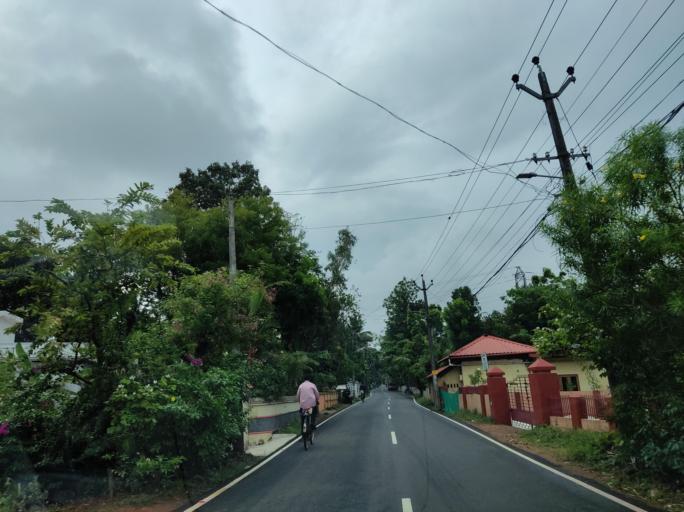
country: IN
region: Kerala
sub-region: Alappuzha
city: Mavelikara
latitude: 9.2423
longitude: 76.5526
